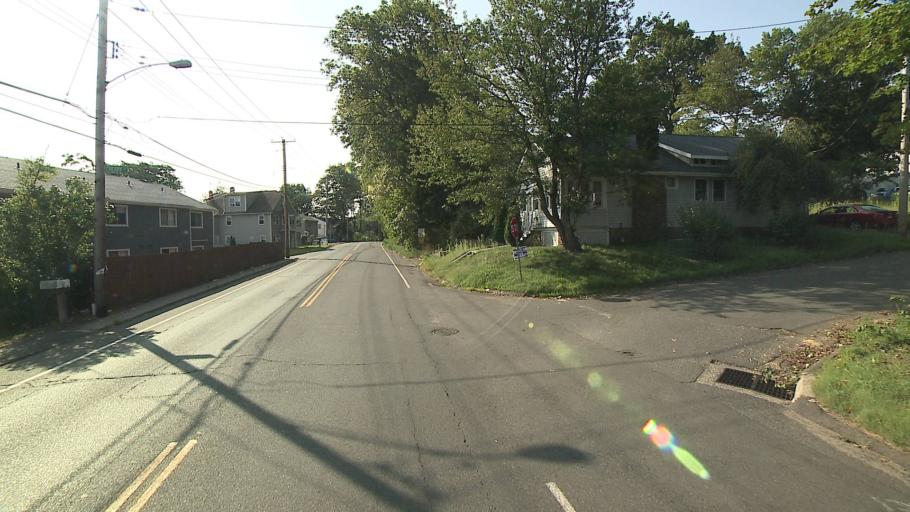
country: US
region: Connecticut
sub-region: New Haven County
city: West Haven
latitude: 41.3008
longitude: -72.9627
